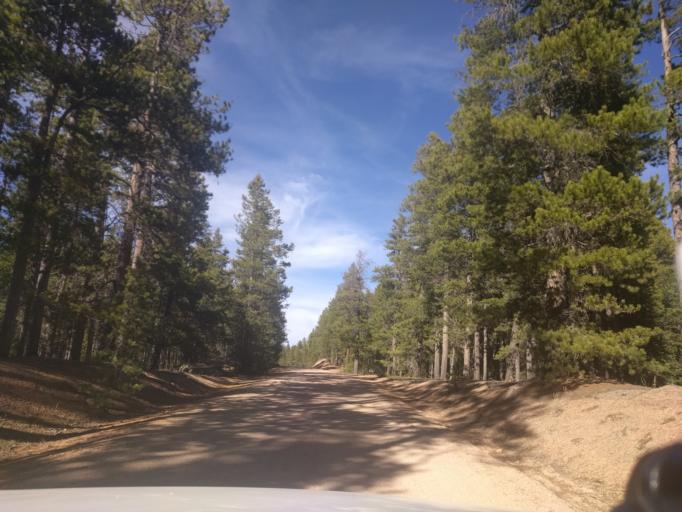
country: US
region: Colorado
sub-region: Douglas County
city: Perry Park
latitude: 39.2169
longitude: -105.0588
